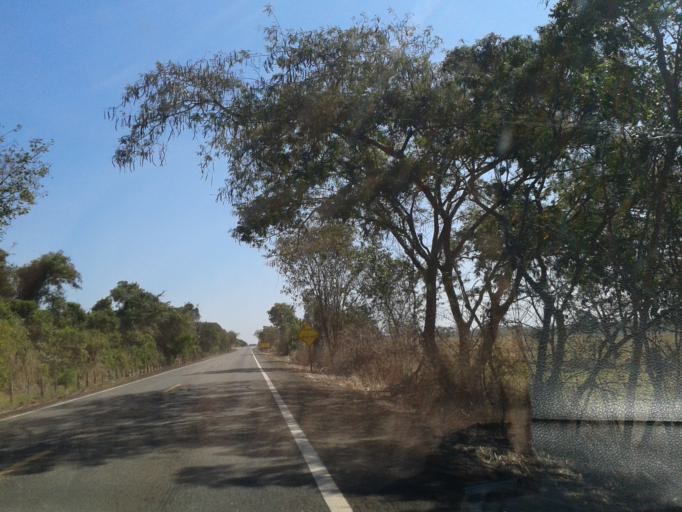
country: BR
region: Goias
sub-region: Sao Miguel Do Araguaia
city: Sao Miguel do Araguaia
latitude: -13.8954
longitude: -50.3276
